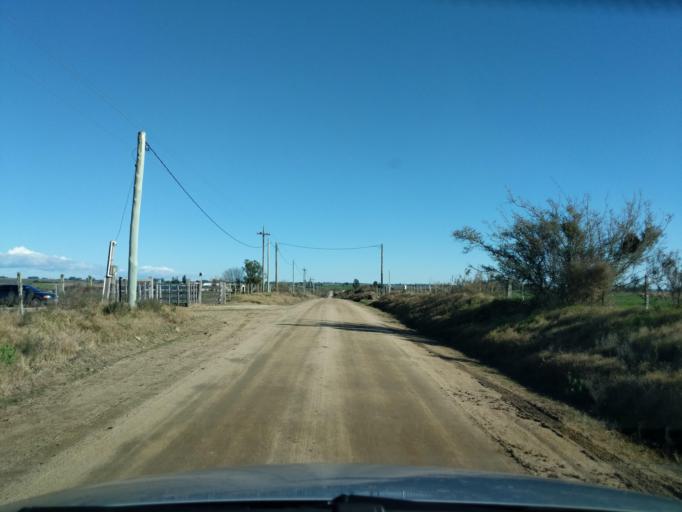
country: UY
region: Florida
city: Florida
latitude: -34.0817
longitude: -56.2535
